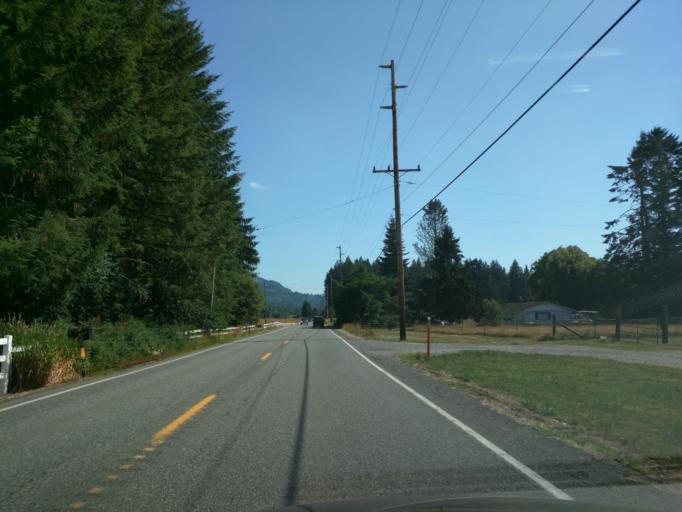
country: US
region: Washington
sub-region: Whatcom County
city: Peaceful Valley
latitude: 48.9111
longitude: -122.1379
